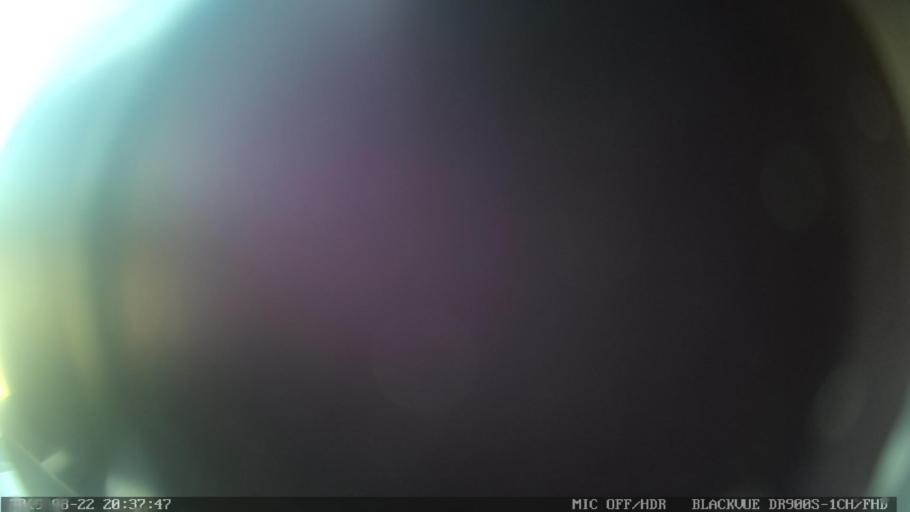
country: PT
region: Portalegre
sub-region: Nisa
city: Nisa
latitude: 39.6775
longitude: -7.7391
